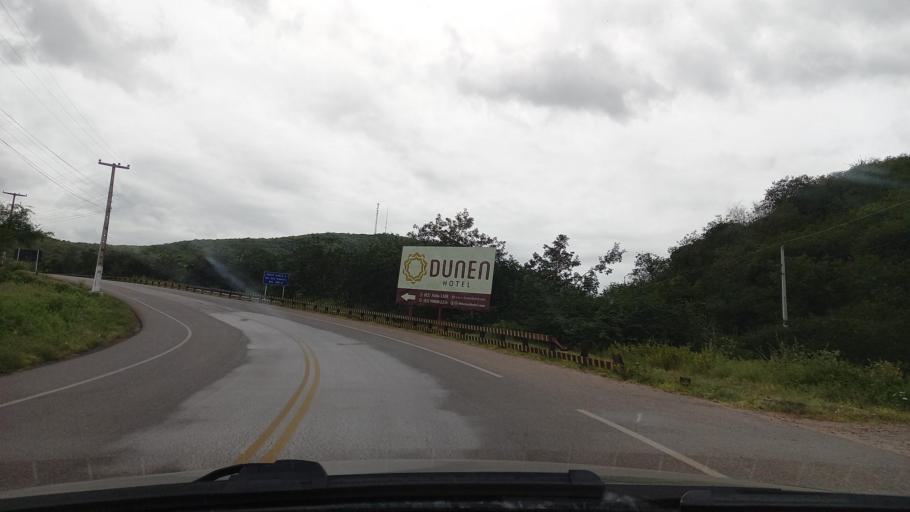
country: BR
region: Sergipe
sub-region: Caninde De Sao Francisco
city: Caninde de Sao Francisco
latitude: -9.6380
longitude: -37.7725
